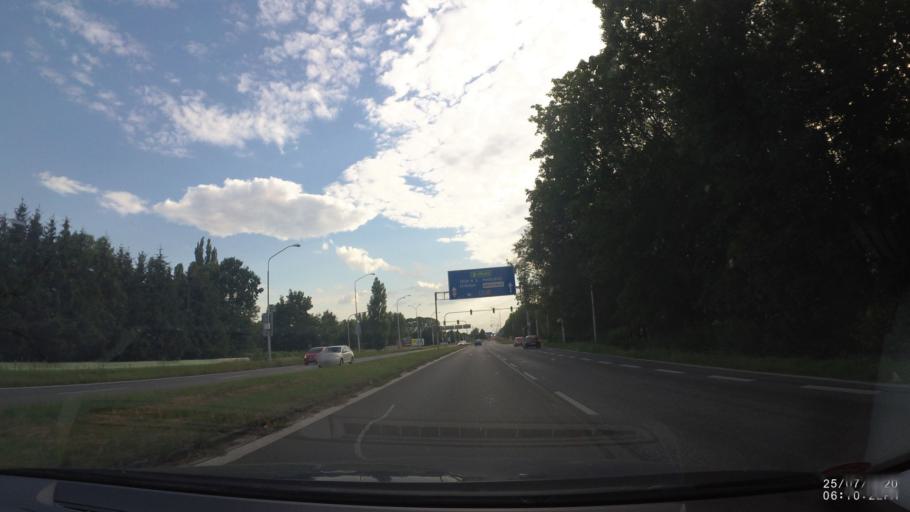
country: CZ
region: Kralovehradecky
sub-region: Okres Hradec Kralove
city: Hradec Kralove
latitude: 50.2004
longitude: 15.8190
